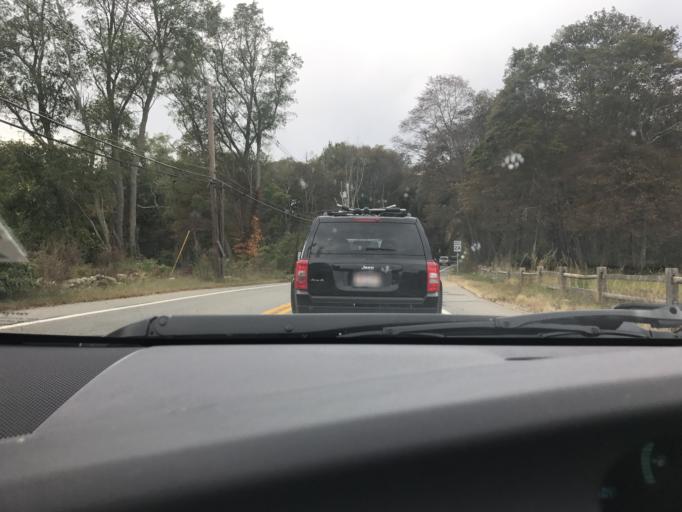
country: US
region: Massachusetts
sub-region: Middlesex County
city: Lincoln
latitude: 42.4486
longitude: -71.2862
